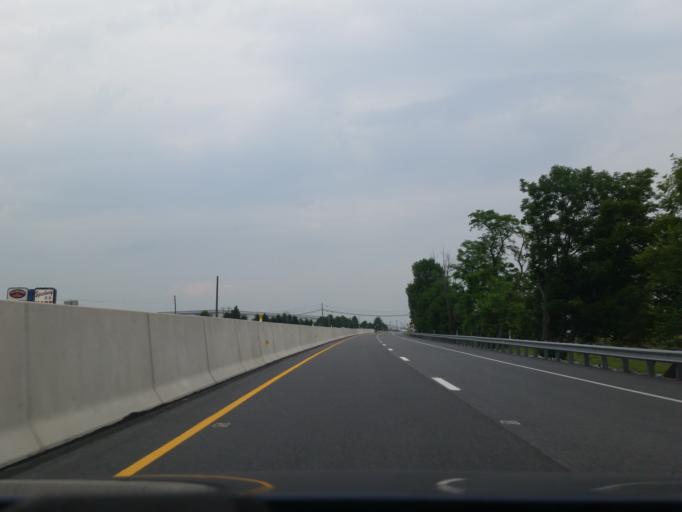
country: US
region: Pennsylvania
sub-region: Lebanon County
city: Fredericksburg
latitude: 40.4415
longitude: -76.4255
